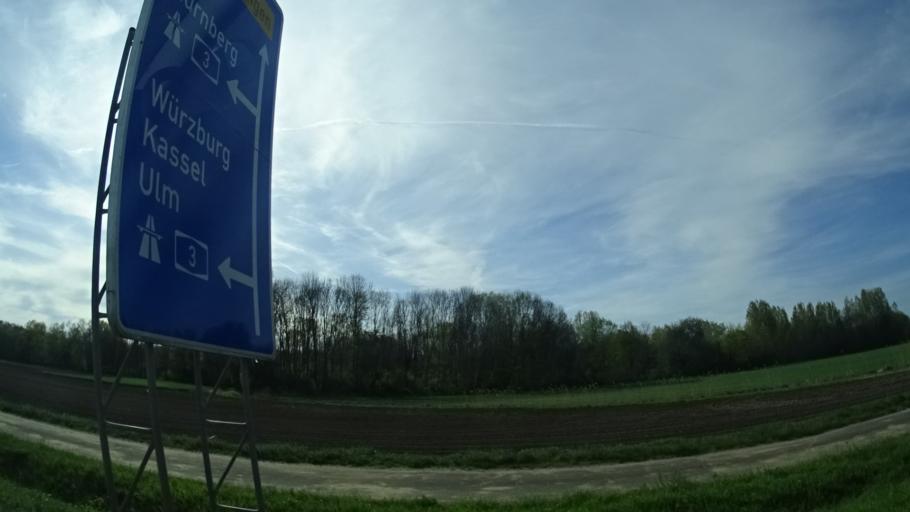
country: DE
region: Bavaria
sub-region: Regierungsbezirk Unterfranken
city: Grosslangheim
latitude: 49.7871
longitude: 10.2132
